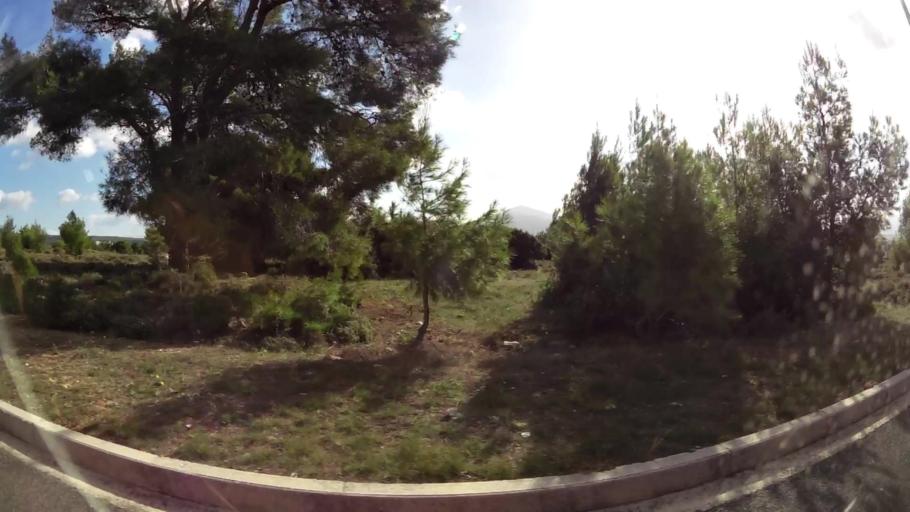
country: GR
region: Attica
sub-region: Nomarchia Anatolikis Attikis
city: Thrakomakedones
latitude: 38.1251
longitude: 23.7670
